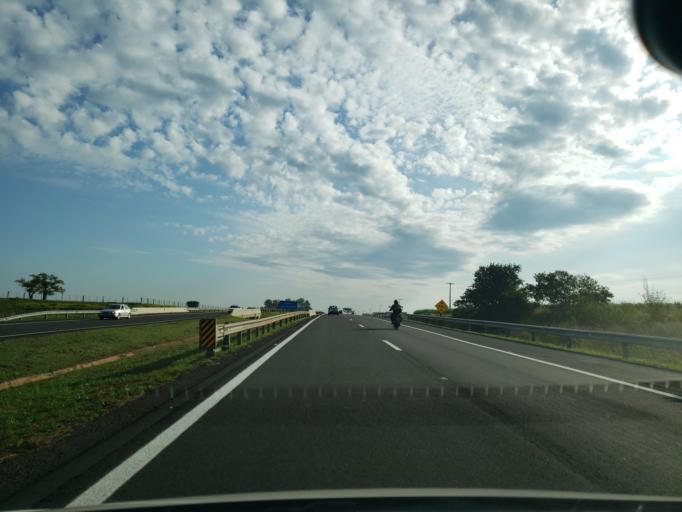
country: BR
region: Sao Paulo
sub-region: Guararapes
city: Guararapes
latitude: -21.2013
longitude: -50.5853
